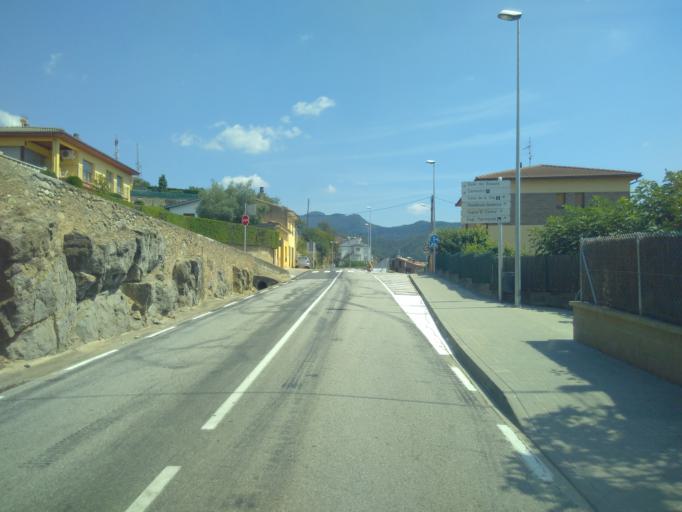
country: ES
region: Catalonia
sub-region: Provincia de Barcelona
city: Montesquiu
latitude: 42.1016
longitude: 2.2199
